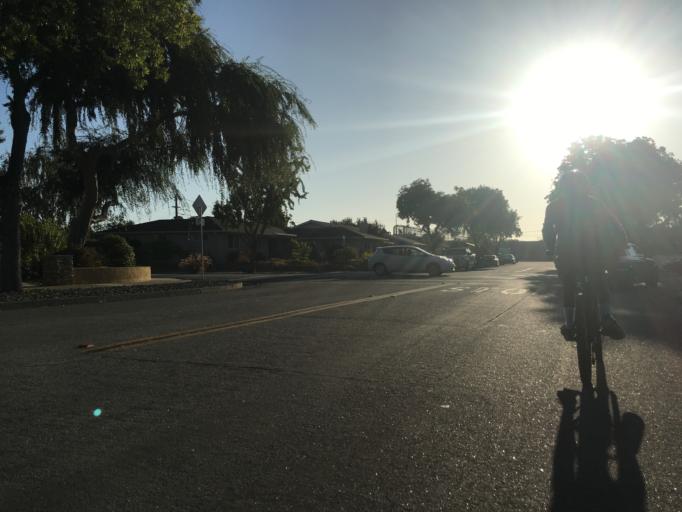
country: US
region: California
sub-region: Santa Clara County
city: Sunnyvale
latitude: 37.3448
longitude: -122.0617
